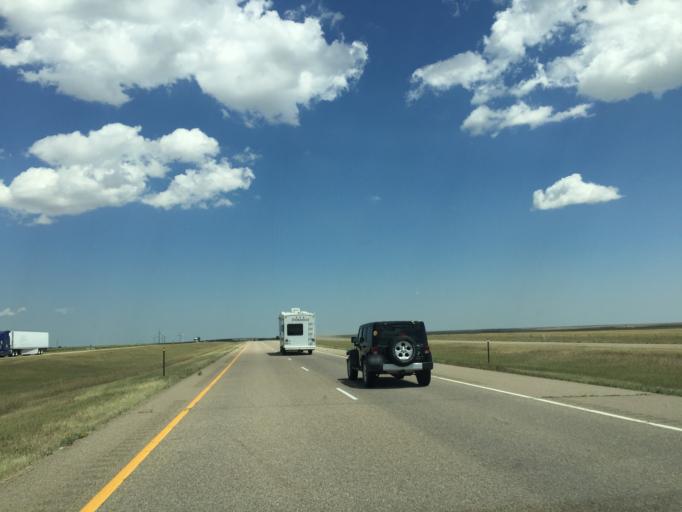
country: US
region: Colorado
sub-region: Lincoln County
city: Hugo
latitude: 39.2770
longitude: -103.4665
